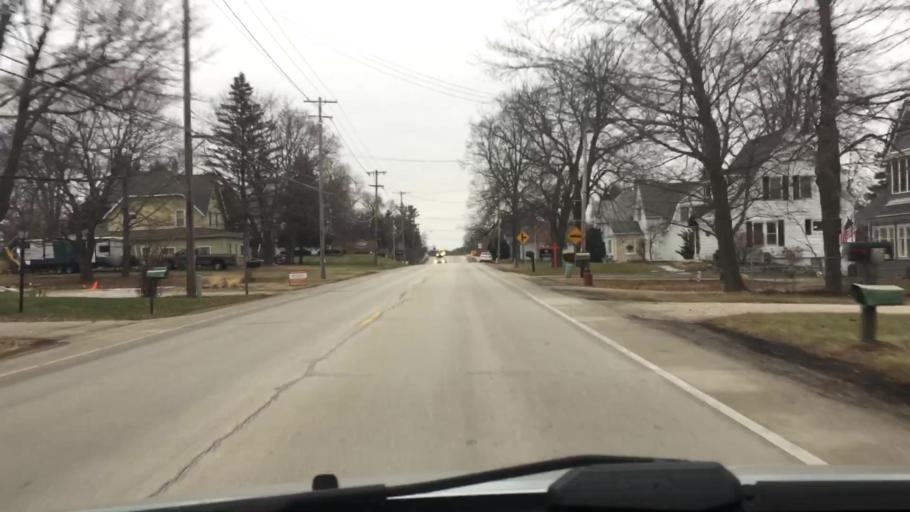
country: US
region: Wisconsin
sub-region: Waukesha County
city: Nashotah
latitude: 43.0962
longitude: -88.4030
